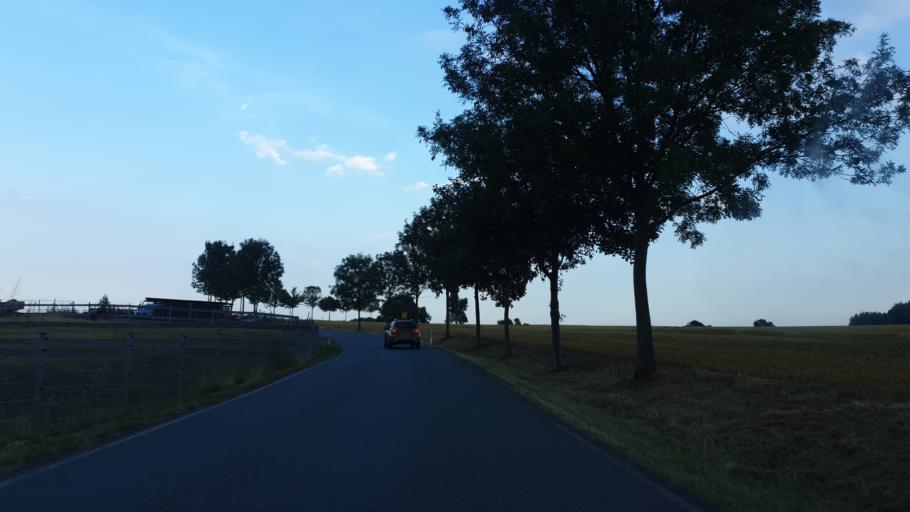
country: DE
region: Saxony
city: Kirchberg
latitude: 50.7899
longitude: 12.7895
